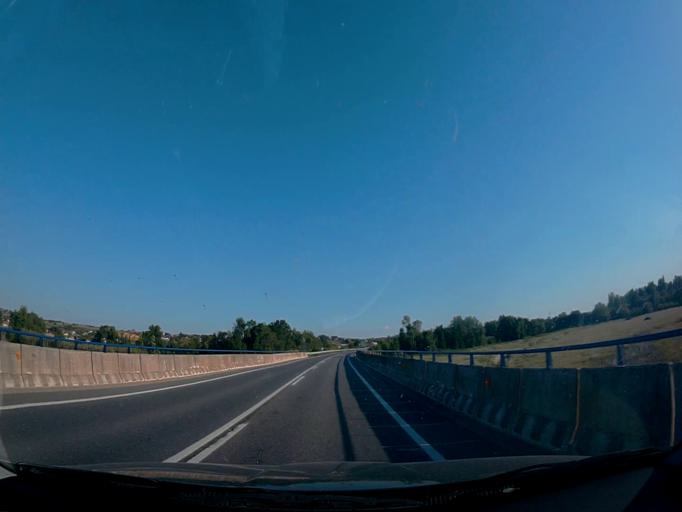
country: ES
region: Castille-La Mancha
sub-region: Province of Toledo
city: Escalona
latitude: 40.1649
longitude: -4.3976
